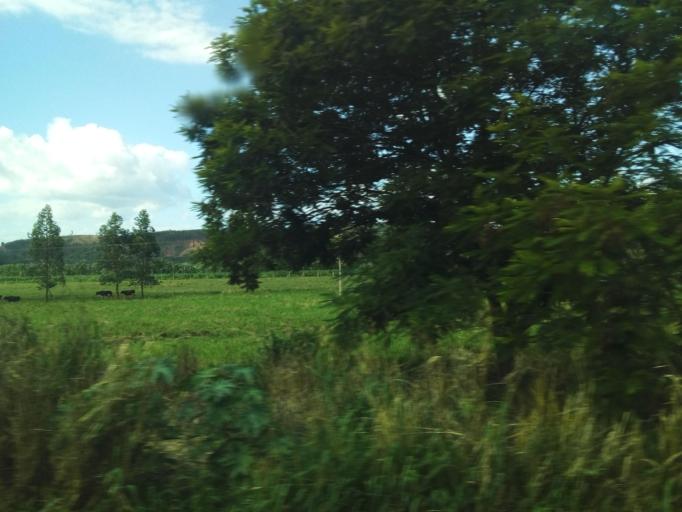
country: BR
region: Minas Gerais
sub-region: Conselheiro Pena
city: Conselheiro Pena
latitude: -18.9852
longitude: -41.6032
